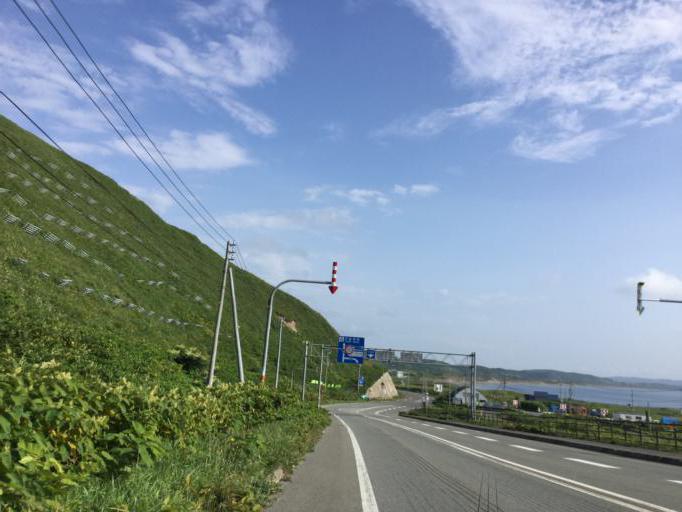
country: JP
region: Hokkaido
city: Wakkanai
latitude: 45.3757
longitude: 141.6554
